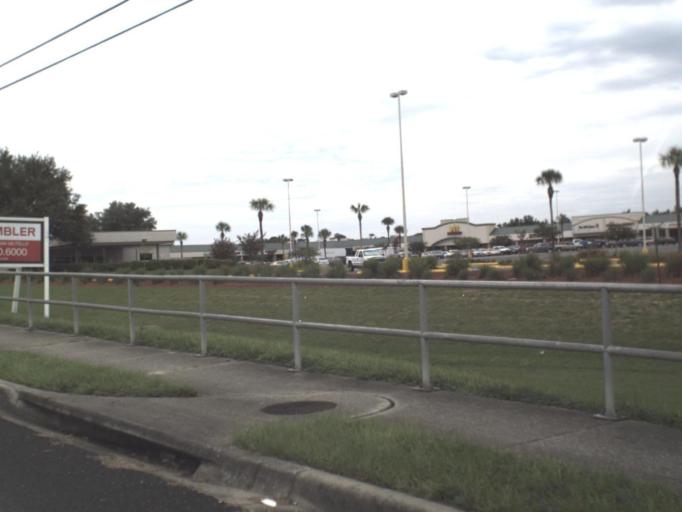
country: US
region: Florida
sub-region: Citrus County
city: Inverness Highlands North
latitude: 28.8539
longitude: -82.3883
